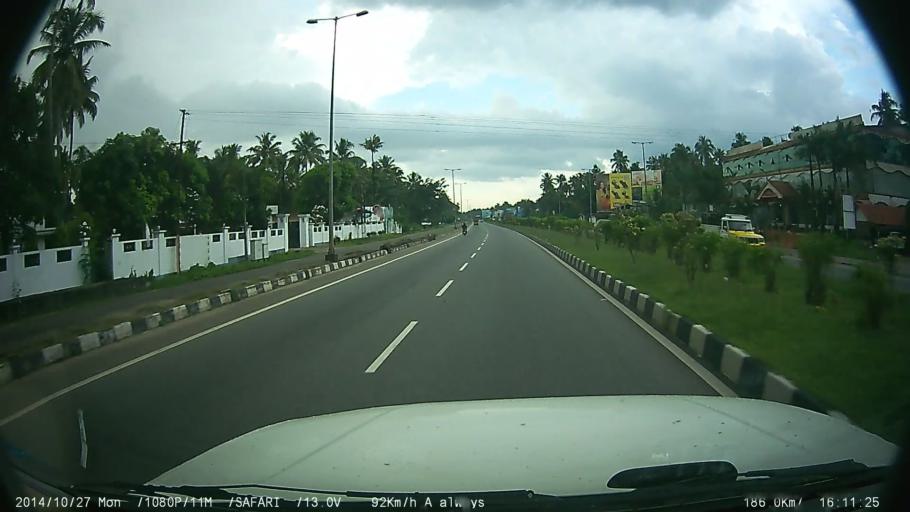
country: IN
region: Kerala
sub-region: Thrissur District
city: Irinjalakuda
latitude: 10.3972
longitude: 76.2851
